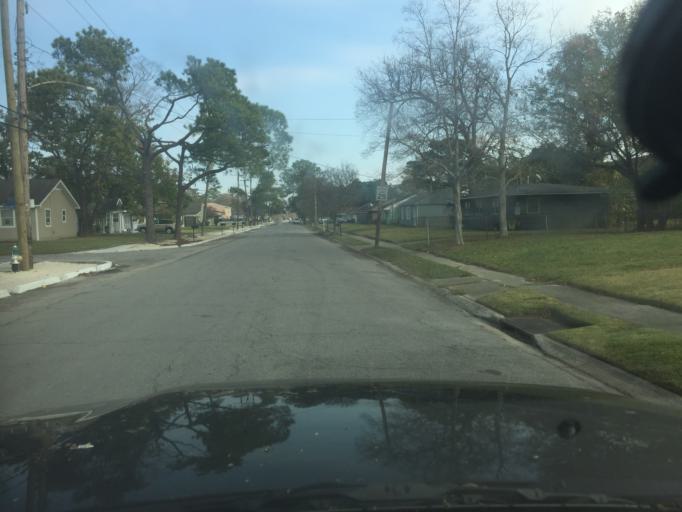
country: US
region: Louisiana
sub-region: Saint Bernard Parish
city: Arabi
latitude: 30.0062
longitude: -90.0392
